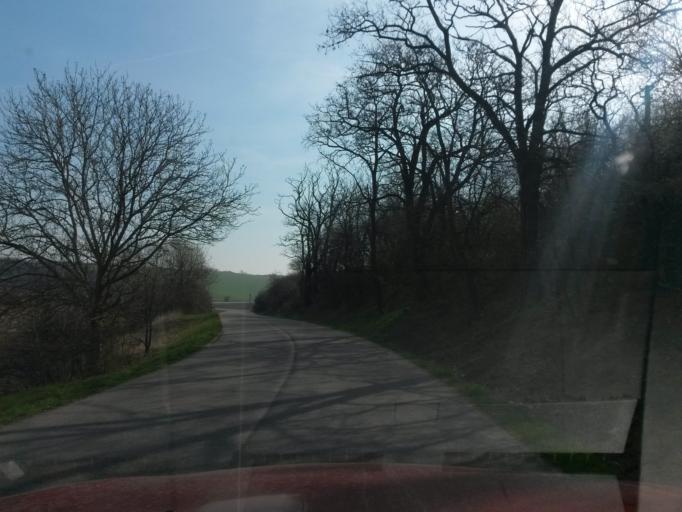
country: SK
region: Nitriansky
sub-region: Okres Nitra
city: Vrable
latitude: 48.1112
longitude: 18.3870
